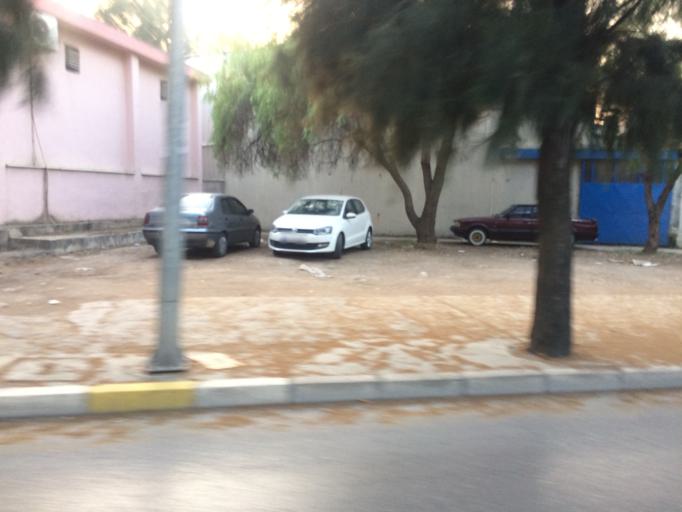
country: TR
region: Izmir
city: Karsiyaka
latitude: 38.4961
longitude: 27.0454
